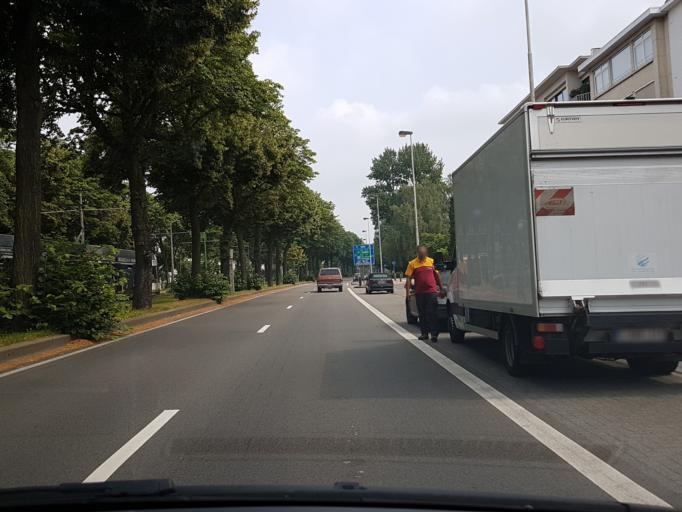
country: BE
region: Flanders
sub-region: Provincie Antwerpen
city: Antwerpen
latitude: 51.1874
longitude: 4.3937
